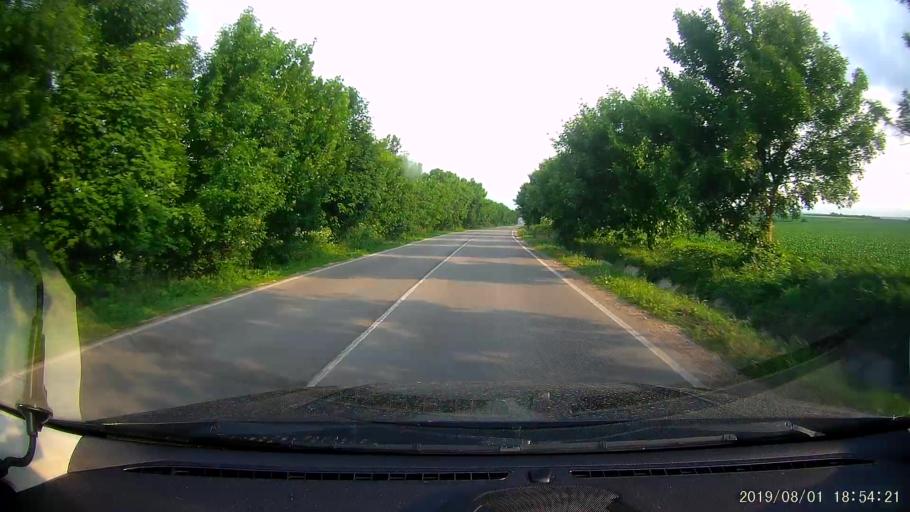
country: BG
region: Shumen
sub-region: Obshtina Shumen
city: Shumen
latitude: 43.2009
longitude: 27.0013
